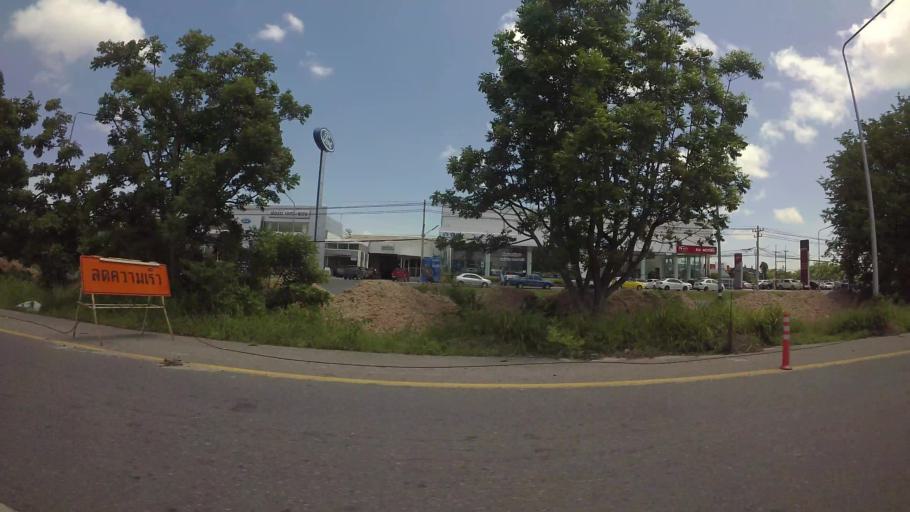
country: TH
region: Rayong
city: Rayong
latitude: 12.7117
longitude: 101.2334
